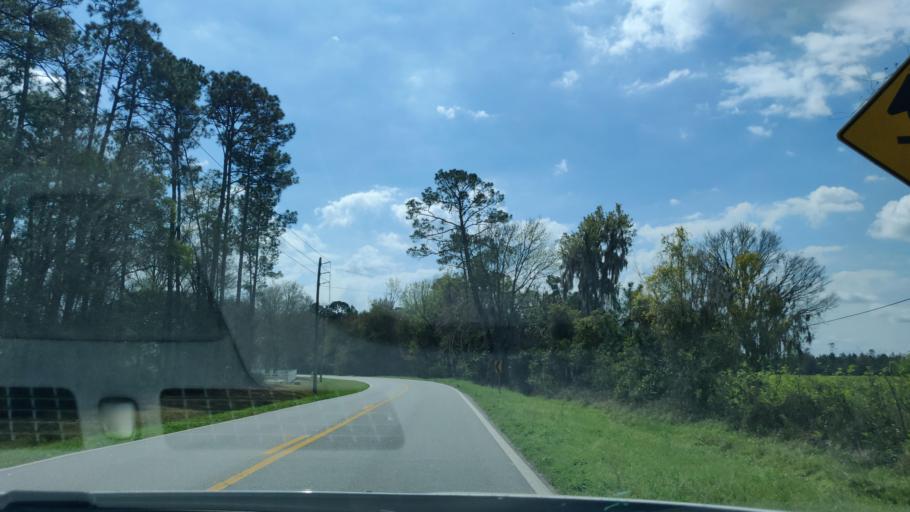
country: US
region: Florida
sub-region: Duval County
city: Baldwin
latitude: 30.2494
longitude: -81.9492
